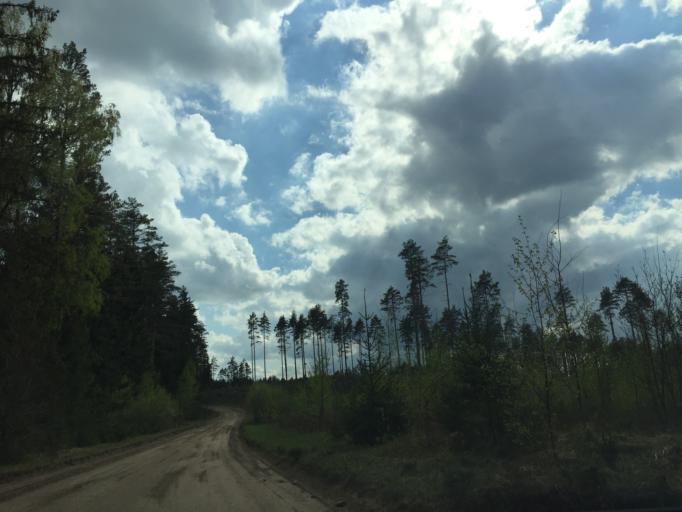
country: LV
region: Sigulda
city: Sigulda
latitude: 57.2968
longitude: 24.8833
